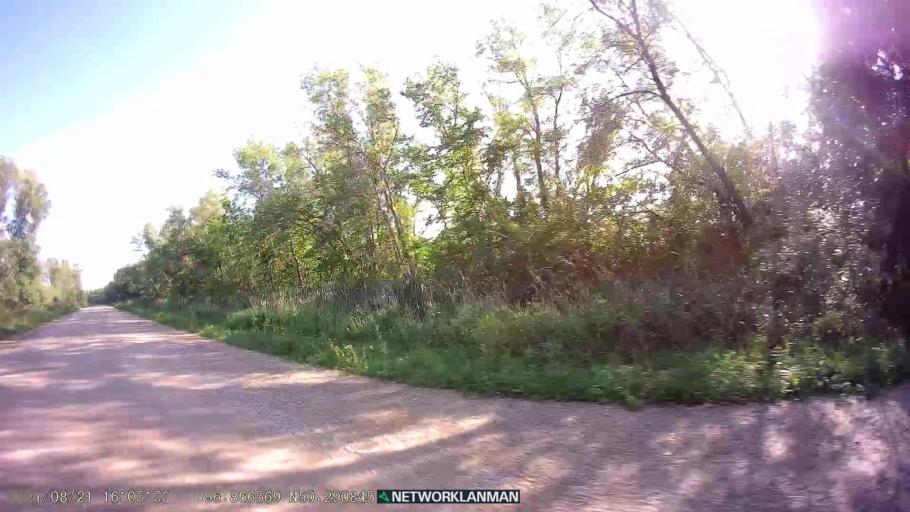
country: CA
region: Manitoba
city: Selkirk
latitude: 50.2905
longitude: -96.8664
